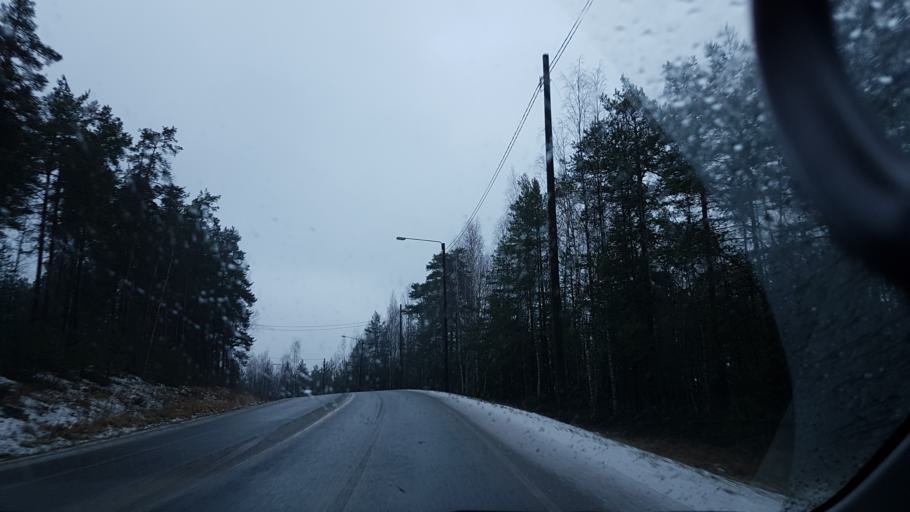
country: FI
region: Uusimaa
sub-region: Helsinki
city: Tuusula
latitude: 60.3594
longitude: 25.0123
